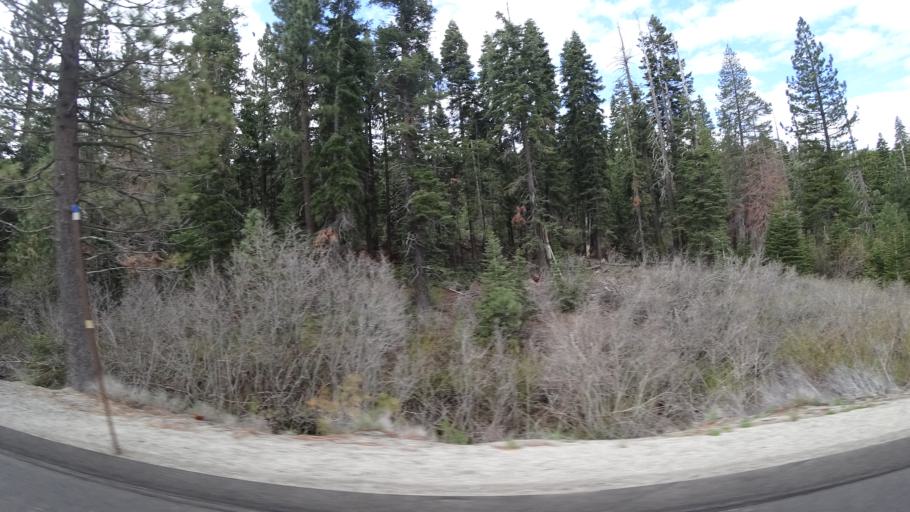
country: US
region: California
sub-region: Placer County
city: Tahoe Vista
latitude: 39.2722
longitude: -120.0977
